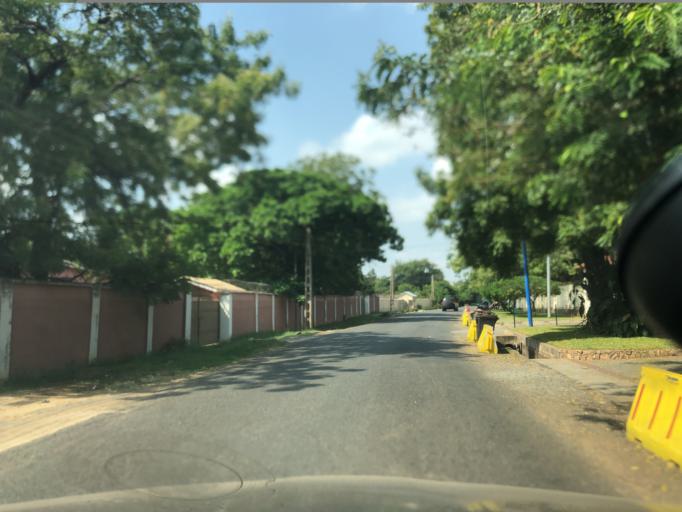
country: GH
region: Greater Accra
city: Accra
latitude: 5.5803
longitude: -0.1723
